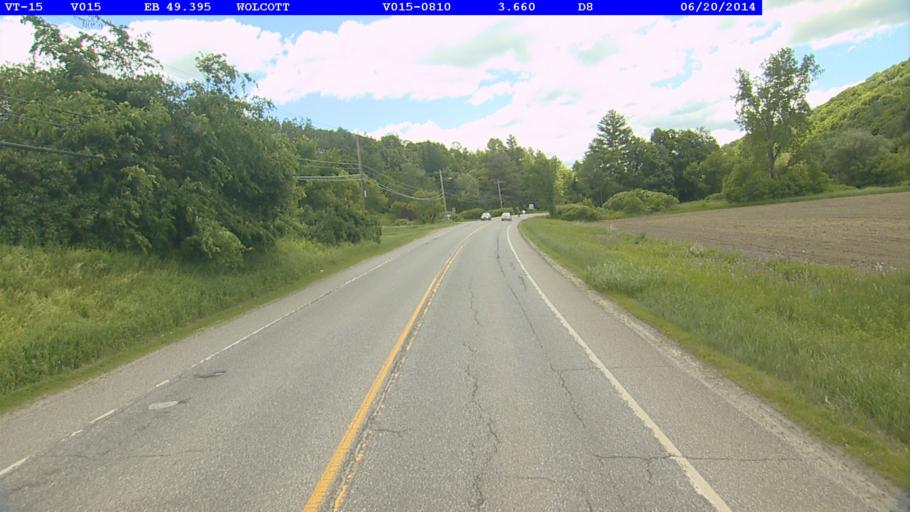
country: US
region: Vermont
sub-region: Caledonia County
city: Hardwick
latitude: 44.5515
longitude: -72.4682
